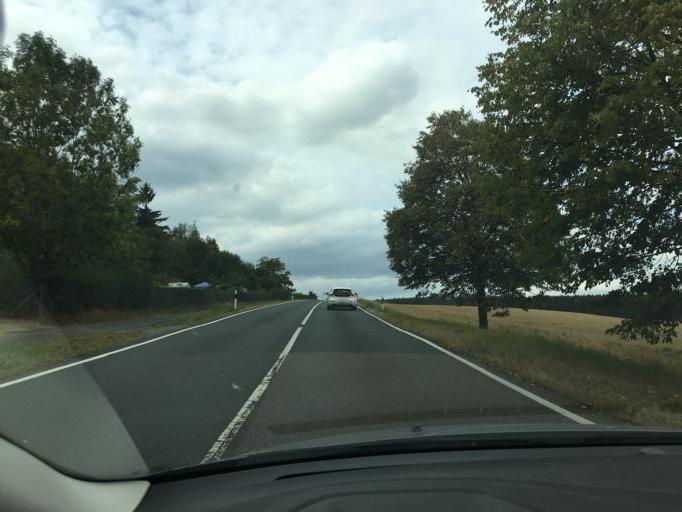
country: DE
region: Thuringia
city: Bad Lobenstein
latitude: 50.4555
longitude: 11.6307
